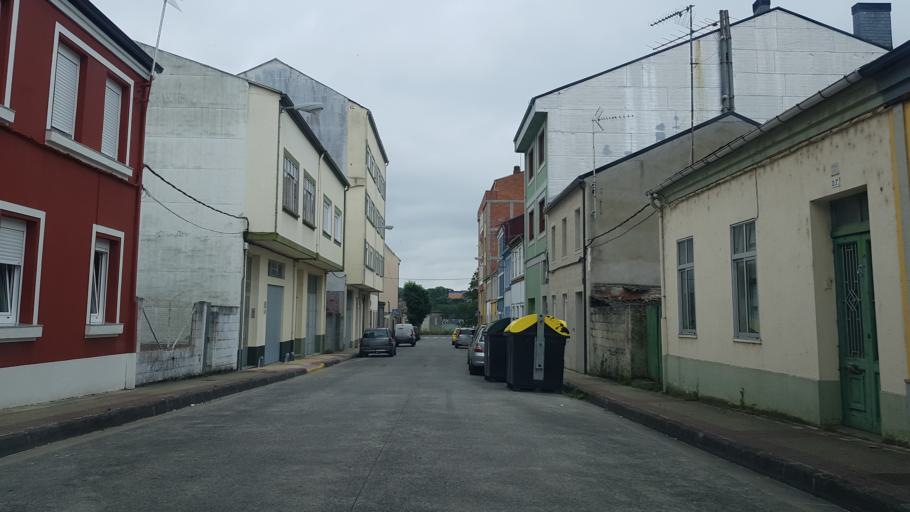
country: ES
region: Galicia
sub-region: Provincia de Lugo
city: Lugo
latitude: 43.0057
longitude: -7.5686
